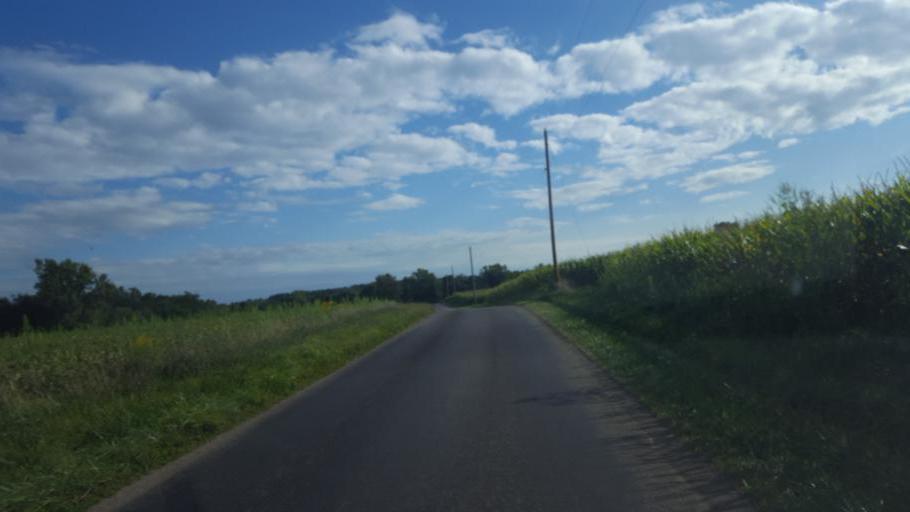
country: US
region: Ohio
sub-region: Knox County
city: Fredericktown
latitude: 40.4322
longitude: -82.5704
